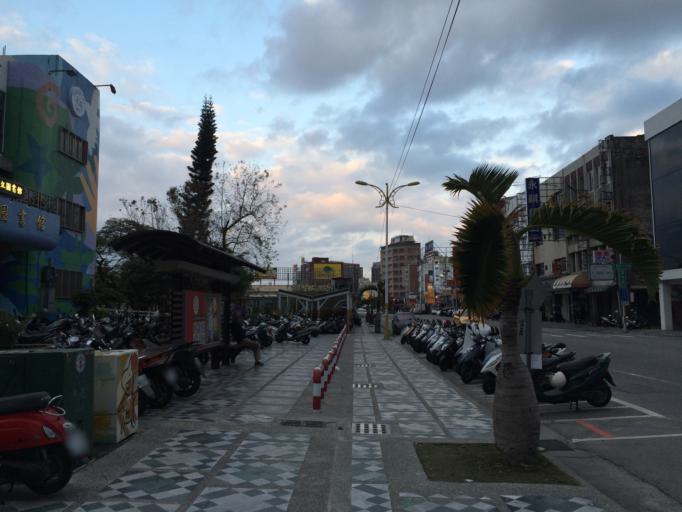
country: TW
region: Taiwan
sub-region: Hualien
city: Hualian
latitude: 23.9900
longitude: 121.6013
